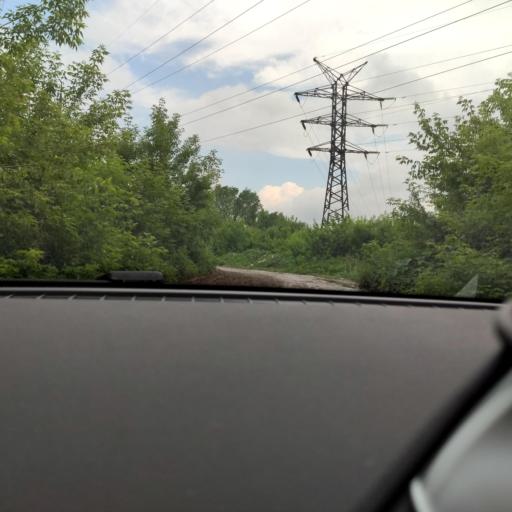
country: RU
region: Samara
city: Petra-Dubrava
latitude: 53.2650
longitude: 50.3000
